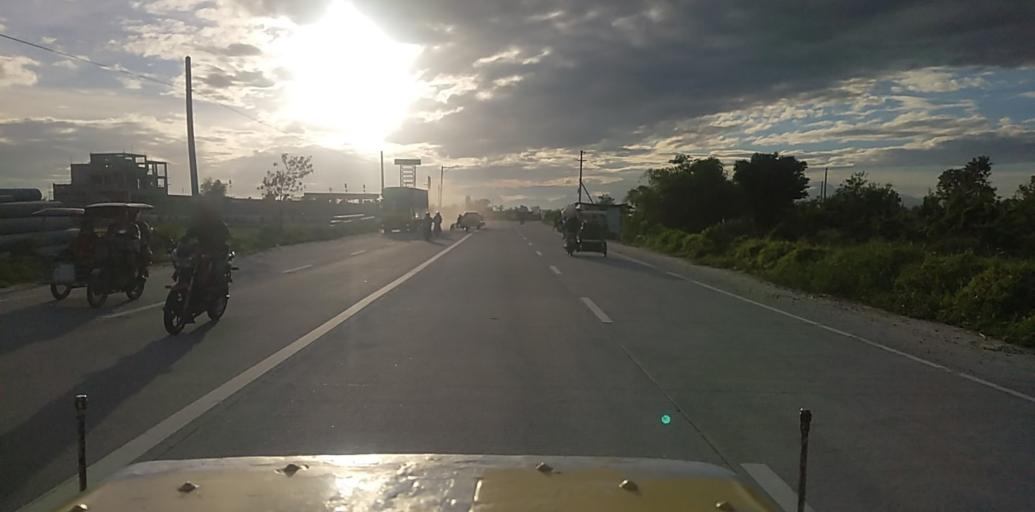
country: PH
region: Central Luzon
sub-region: Province of Pampanga
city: Anao
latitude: 15.1346
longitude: 120.6830
